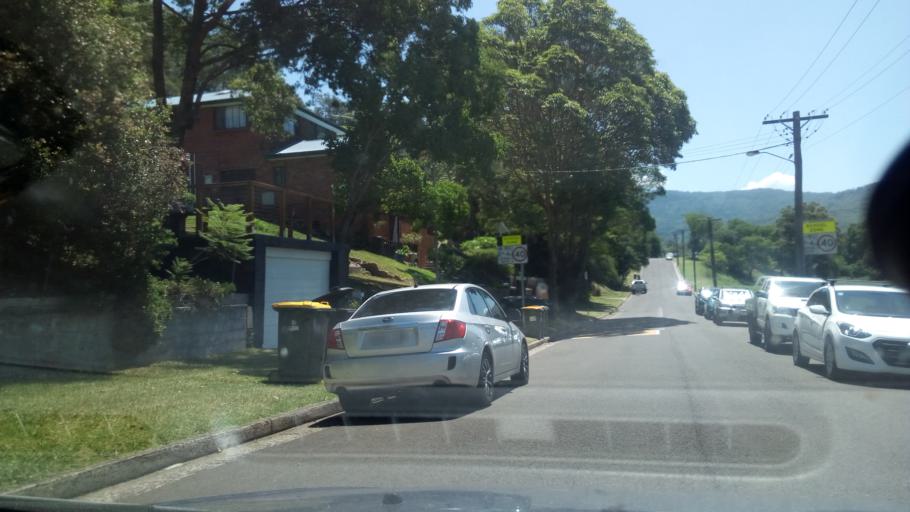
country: AU
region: New South Wales
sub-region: Wollongong
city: West Wollongong
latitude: -34.4311
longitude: 150.8602
